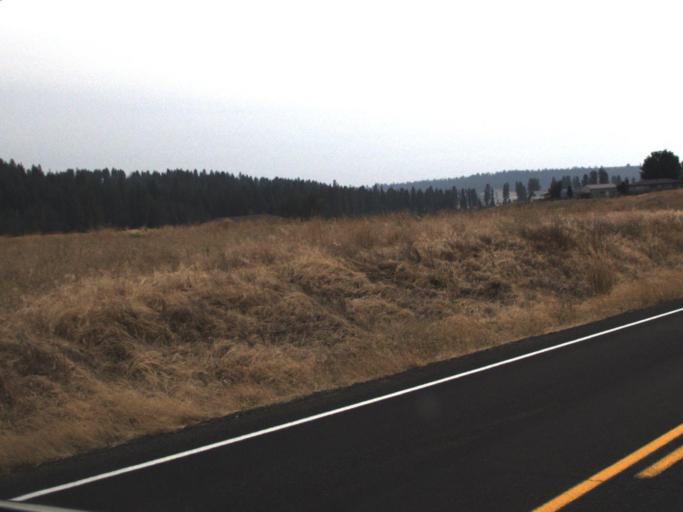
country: US
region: Washington
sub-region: Spokane County
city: Trentwood
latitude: 47.7955
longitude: -117.2452
